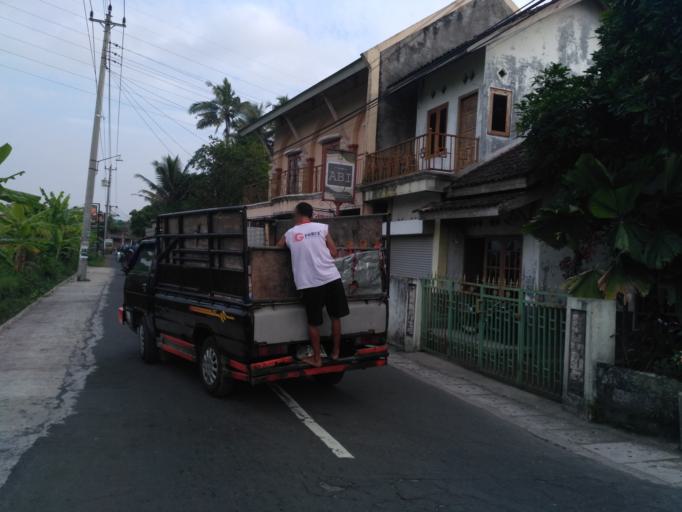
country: ID
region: Daerah Istimewa Yogyakarta
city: Melati
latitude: -7.7099
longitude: 110.3886
